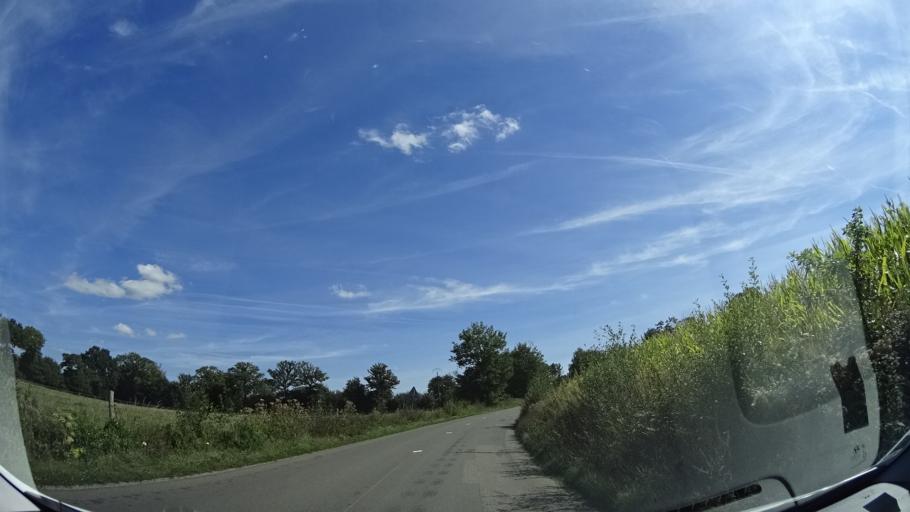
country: FR
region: Brittany
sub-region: Departement d'Ille-et-Vilaine
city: Saint-Sulpice-la-Foret
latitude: 48.2188
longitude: -1.5662
